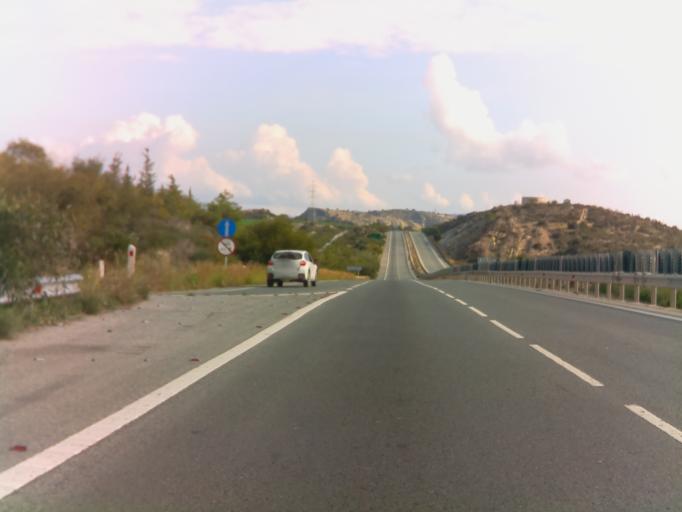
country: CY
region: Limassol
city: Pyrgos
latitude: 34.7228
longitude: 33.2688
